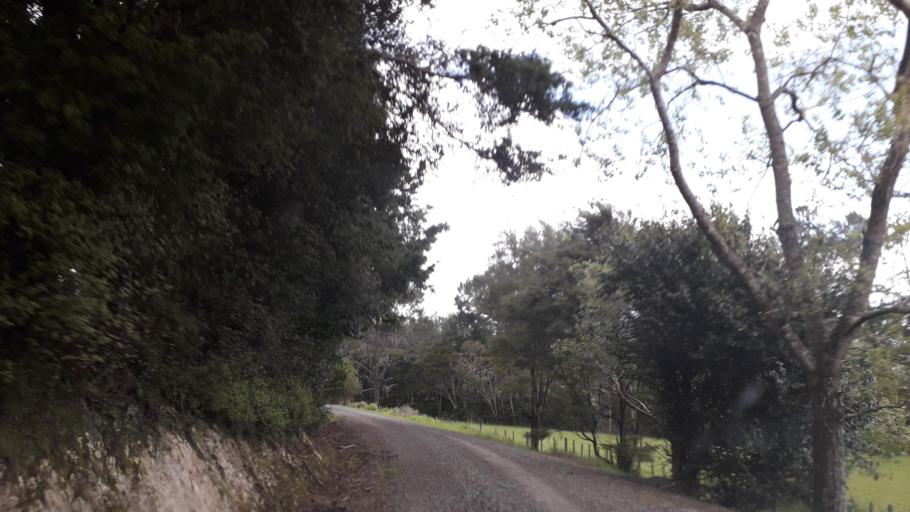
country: NZ
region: Northland
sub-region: Far North District
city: Waimate North
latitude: -35.3184
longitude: 173.5750
